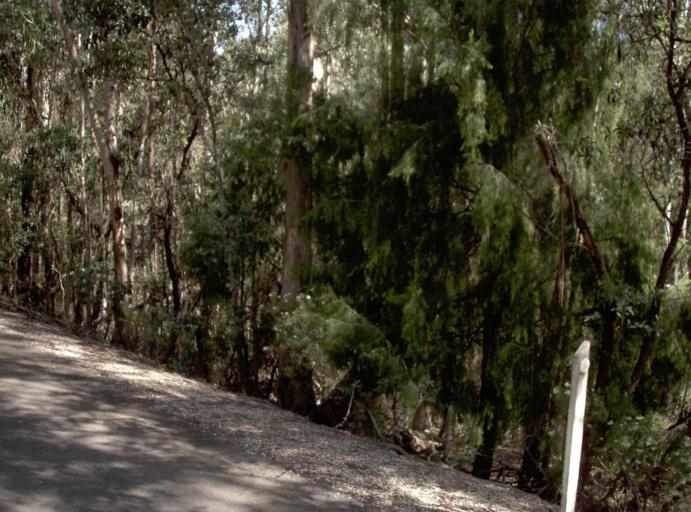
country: AU
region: Victoria
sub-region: East Gippsland
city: Lakes Entrance
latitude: -37.4202
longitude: 148.1269
